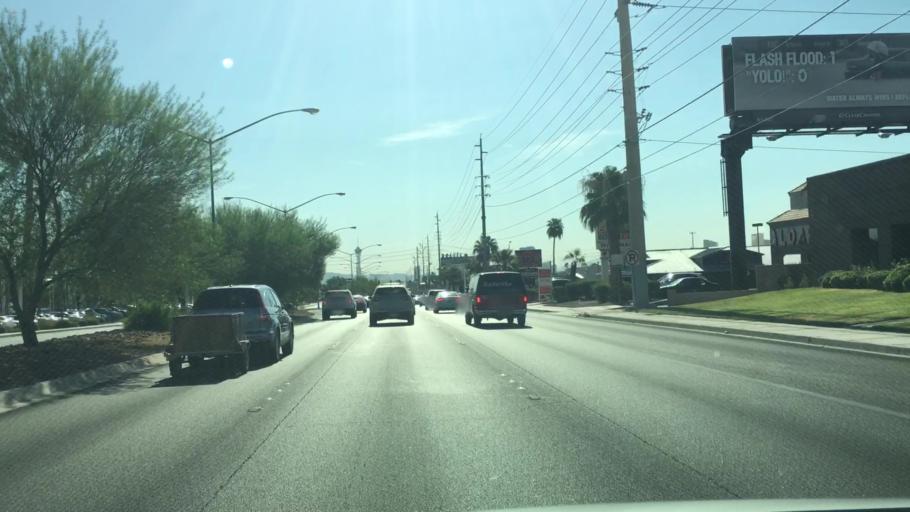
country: US
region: Nevada
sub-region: Clark County
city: Spring Valley
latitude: 36.1442
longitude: -115.2204
